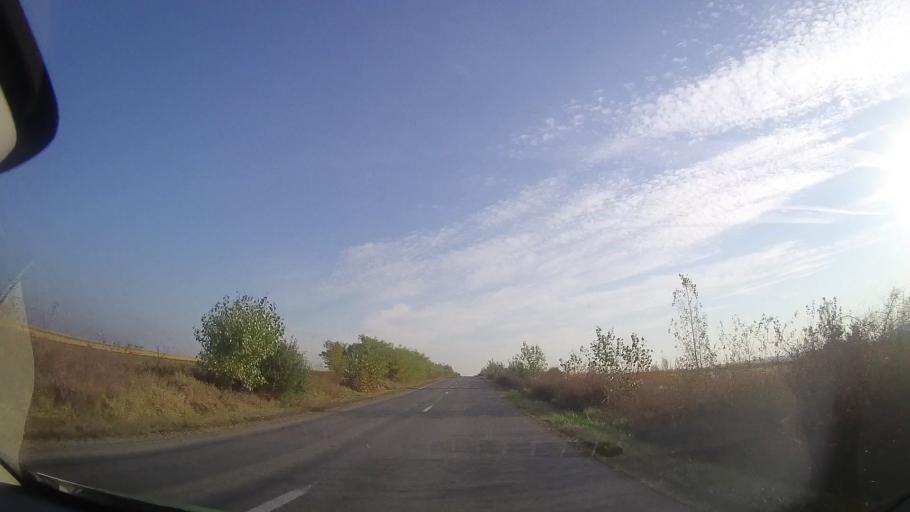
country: RO
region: Timis
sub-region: Comuna Fibis
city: Fibis
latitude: 45.9837
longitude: 21.4342
